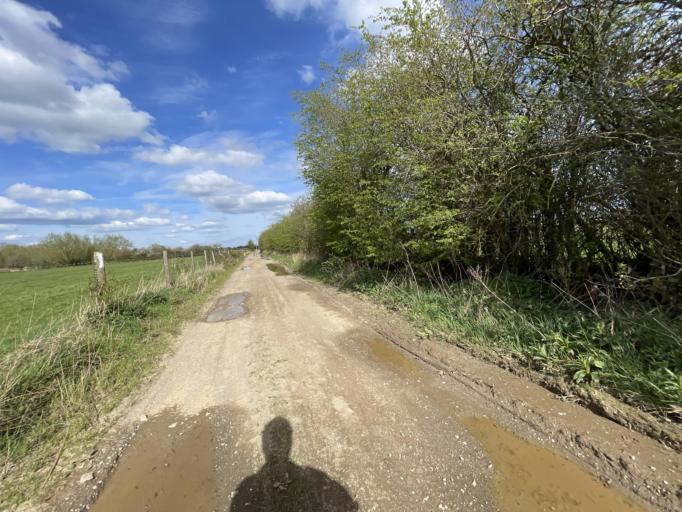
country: GB
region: England
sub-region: Warwickshire
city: Rugby
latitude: 52.3750
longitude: -1.1929
